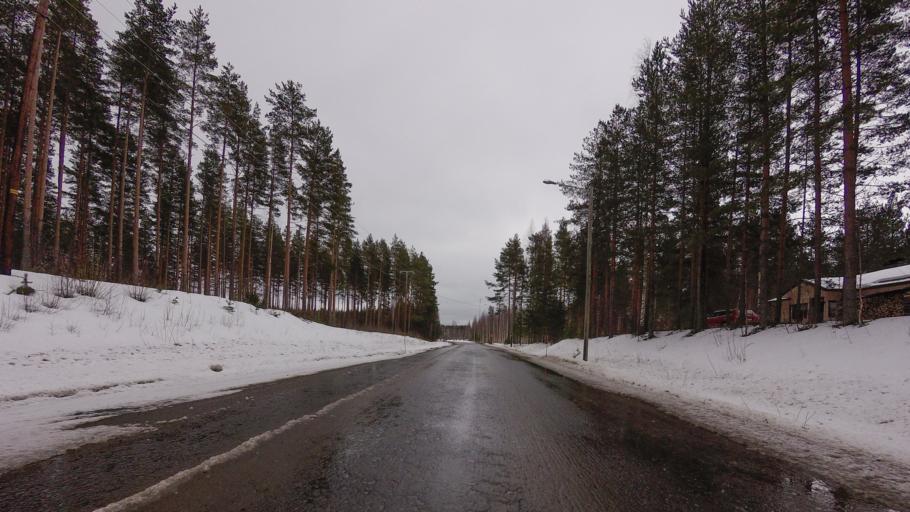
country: FI
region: Southern Savonia
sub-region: Savonlinna
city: Rantasalmi
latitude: 62.1107
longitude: 28.6116
